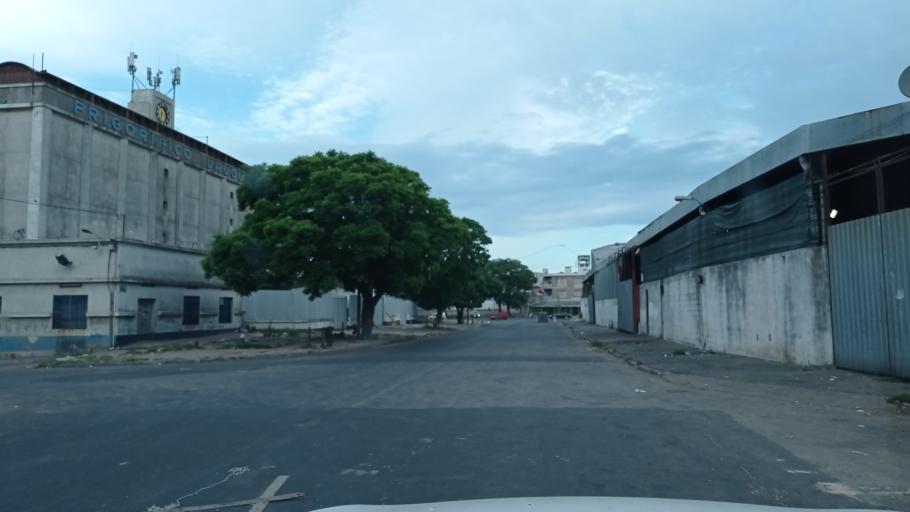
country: UY
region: Montevideo
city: Montevideo
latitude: -34.8712
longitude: -56.1538
